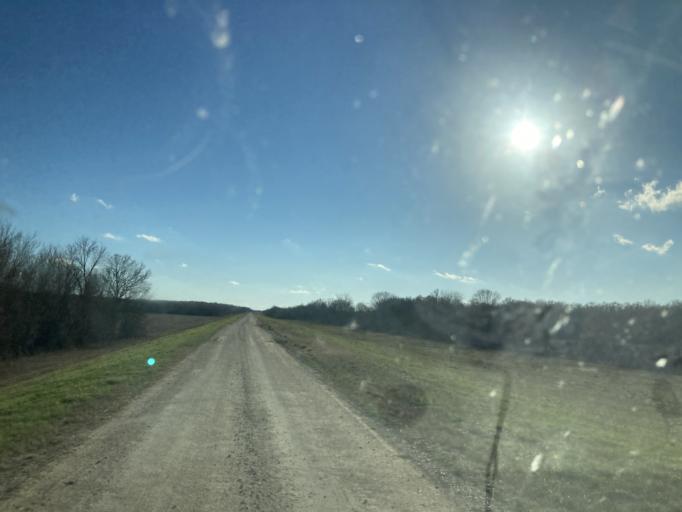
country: US
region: Mississippi
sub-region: Yazoo County
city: Yazoo City
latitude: 32.9345
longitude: -90.5472
